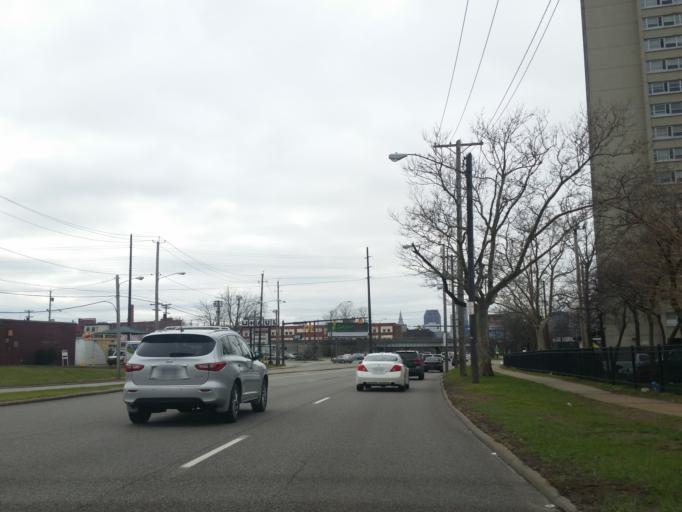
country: US
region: Ohio
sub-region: Cuyahoga County
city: Bratenahl
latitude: 41.5064
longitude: -81.6503
